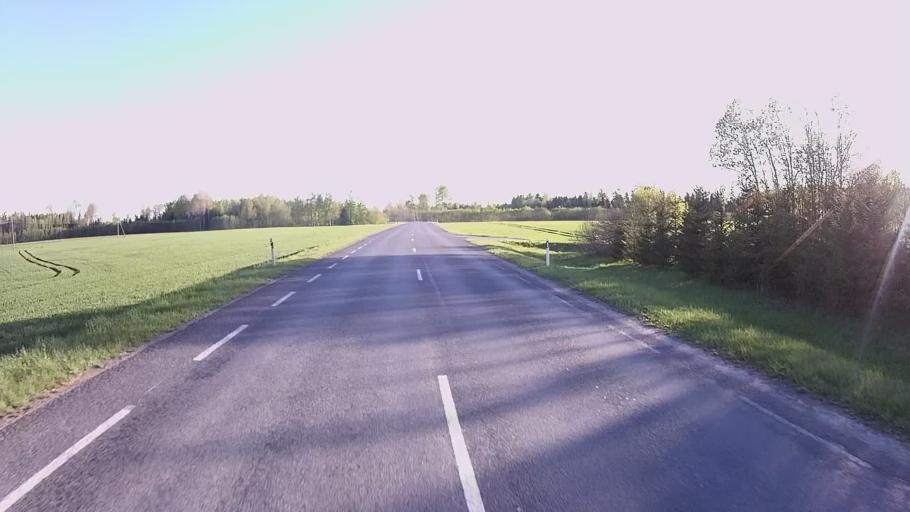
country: EE
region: Viljandimaa
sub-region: Viiratsi vald
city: Viiratsi
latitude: 58.4350
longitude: 25.7255
